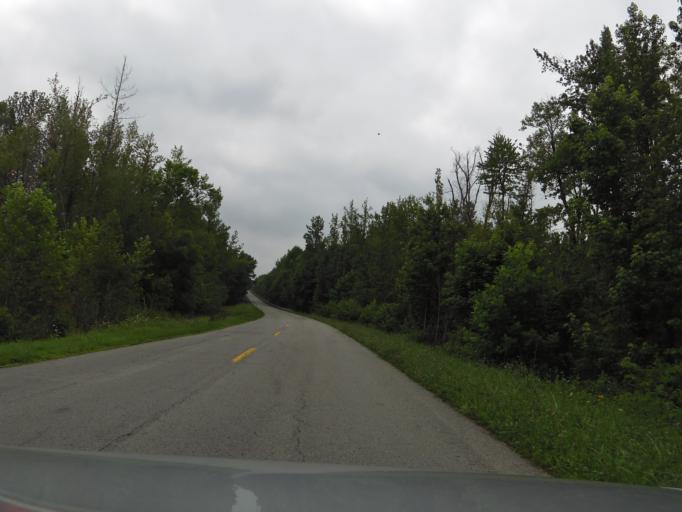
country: US
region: Kentucky
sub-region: Muhlenberg County
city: Morehead
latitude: 37.2835
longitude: -87.3023
